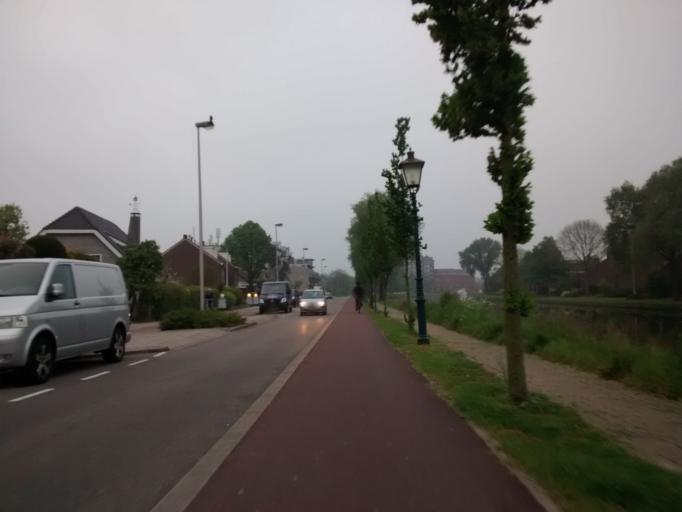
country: NL
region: South Holland
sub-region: Gemeente Leiderdorp
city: Leiderdorp
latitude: 52.1592
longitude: 4.5178
